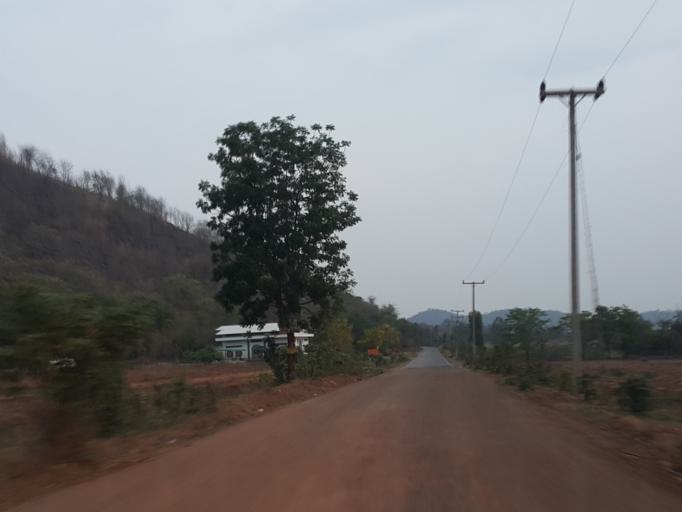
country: TH
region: Suphan Buri
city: Dan Chang
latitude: 14.8751
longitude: 99.6622
